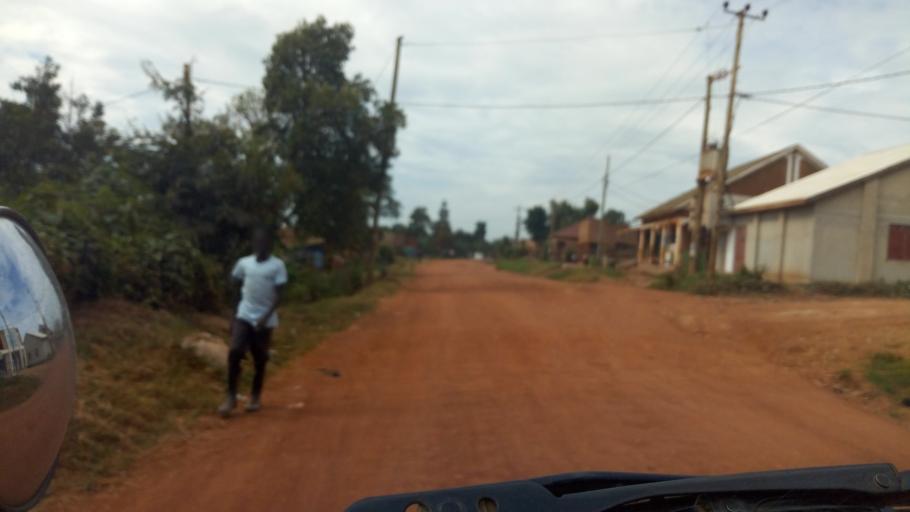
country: UG
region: Central Region
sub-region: Wakiso District
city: Bweyogerere
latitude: 0.3561
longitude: 32.7003
